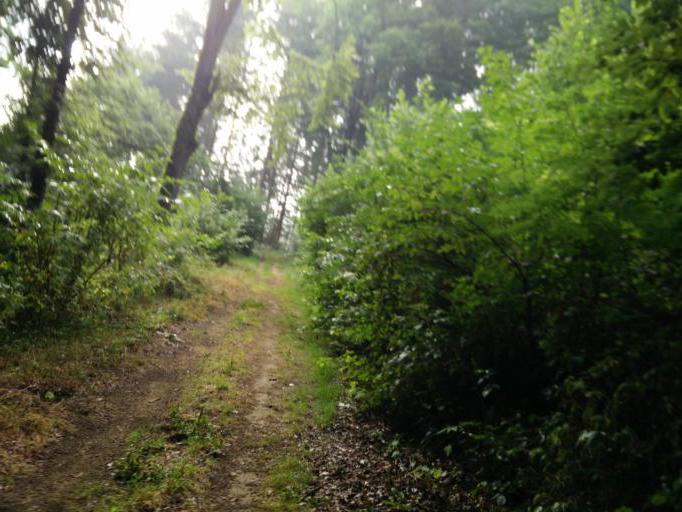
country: LU
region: Luxembourg
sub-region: Canton de Capellen
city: Mamer
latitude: 49.6406
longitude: 6.0446
